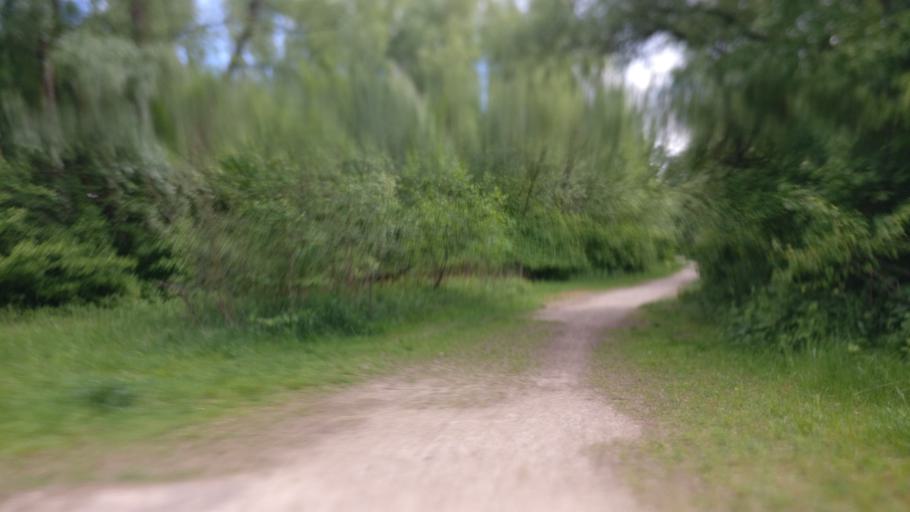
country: DE
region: North Rhine-Westphalia
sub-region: Regierungsbezirk Detmold
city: Lage
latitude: 52.0092
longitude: 8.7647
